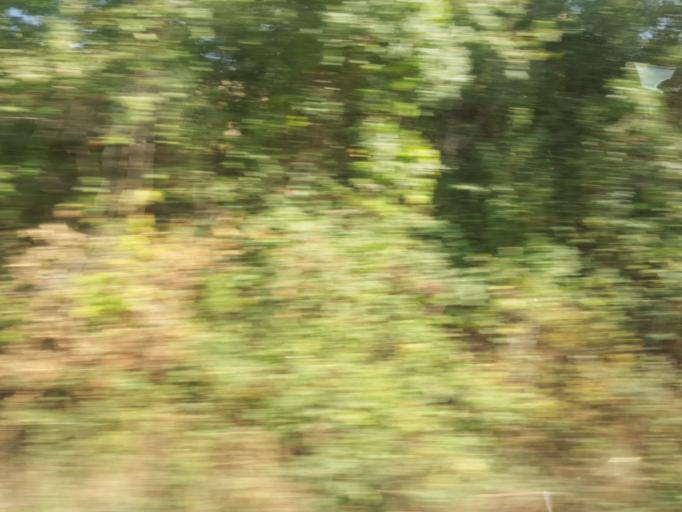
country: TR
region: Tokat
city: Artova
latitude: 40.0625
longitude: 36.2988
